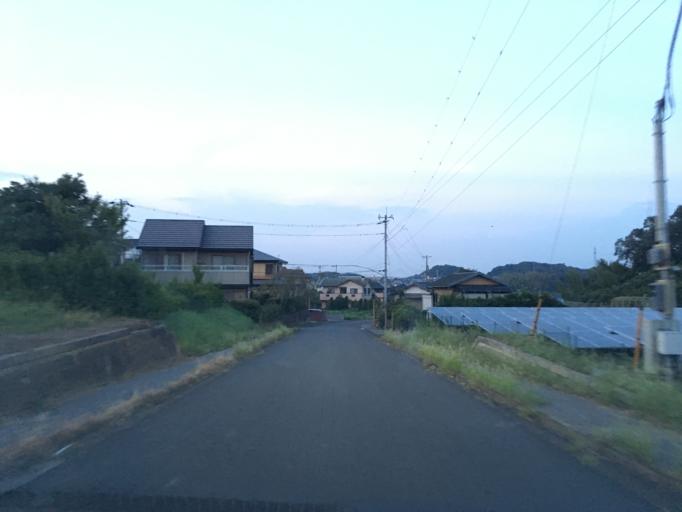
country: JP
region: Chiba
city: Kimitsu
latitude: 35.3399
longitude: 139.9106
